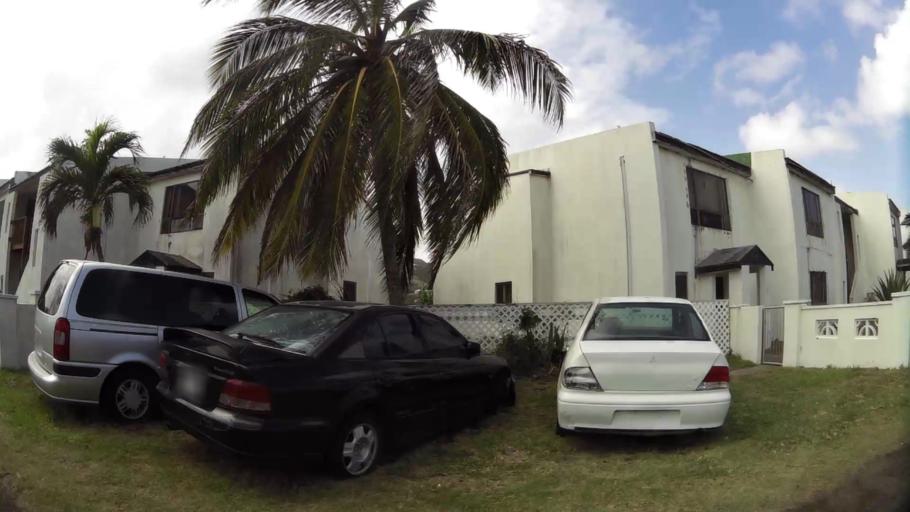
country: KN
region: Saint George Basseterre
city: Basseterre
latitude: 17.2893
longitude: -62.6860
